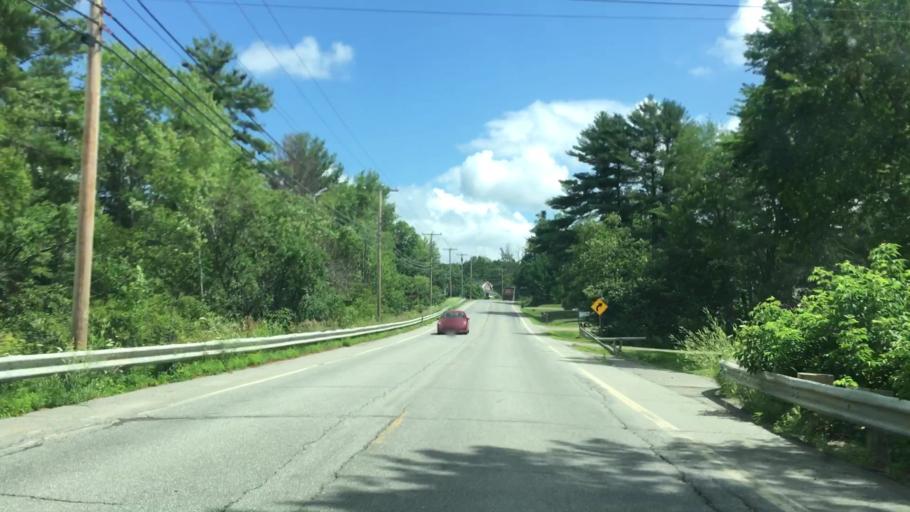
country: US
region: Maine
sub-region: Penobscot County
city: Carmel
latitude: 44.8009
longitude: -69.0390
